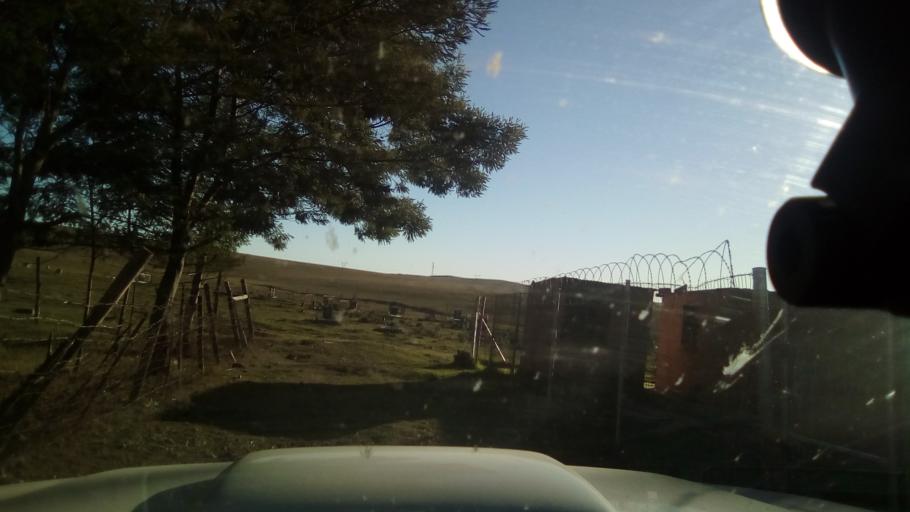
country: ZA
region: Eastern Cape
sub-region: Buffalo City Metropolitan Municipality
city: Bhisho
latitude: -32.9512
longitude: 27.2917
